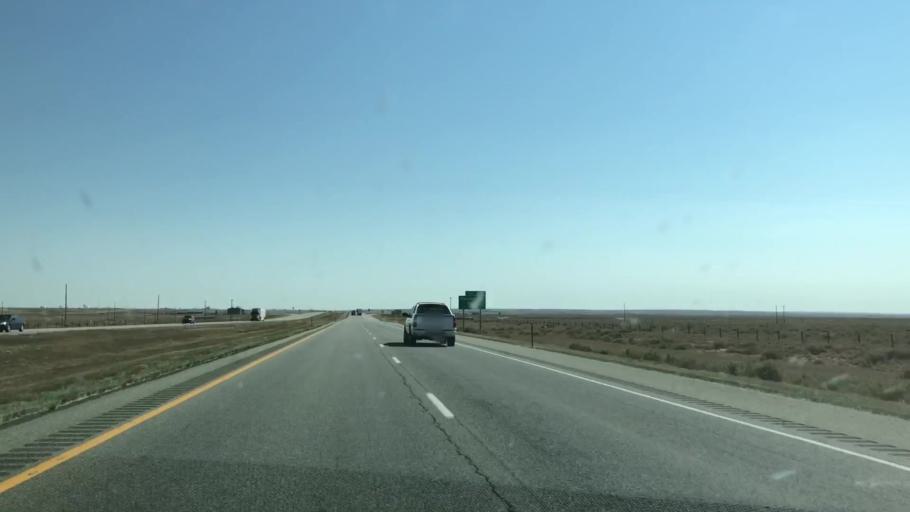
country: US
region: Wyoming
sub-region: Carbon County
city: Rawlins
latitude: 41.6637
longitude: -108.0431
